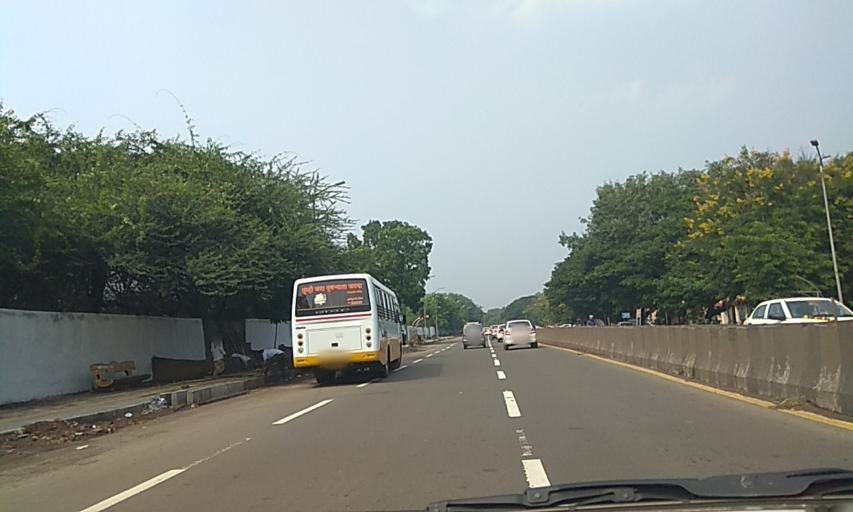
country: IN
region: Maharashtra
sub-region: Pune Division
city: Khadki
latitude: 18.5525
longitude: 73.8768
